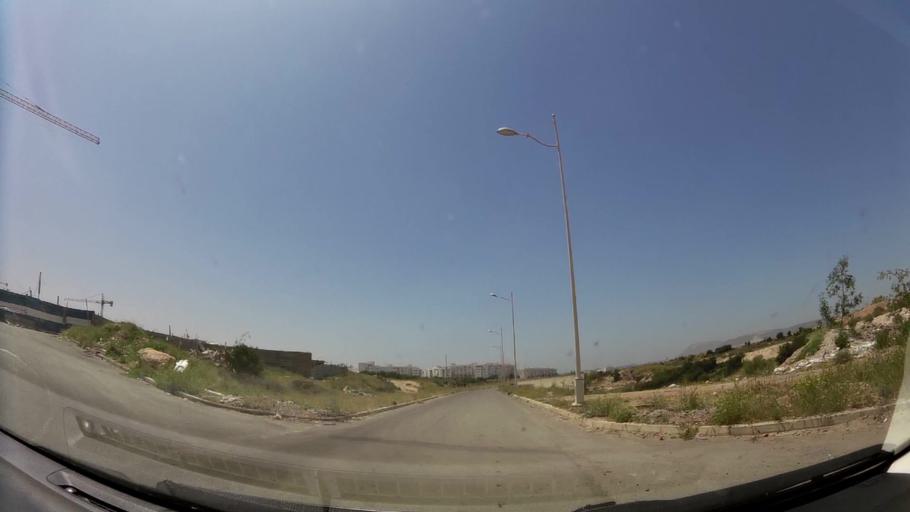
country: MA
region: Oued ed Dahab-Lagouira
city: Dakhla
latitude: 30.4405
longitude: -9.5655
